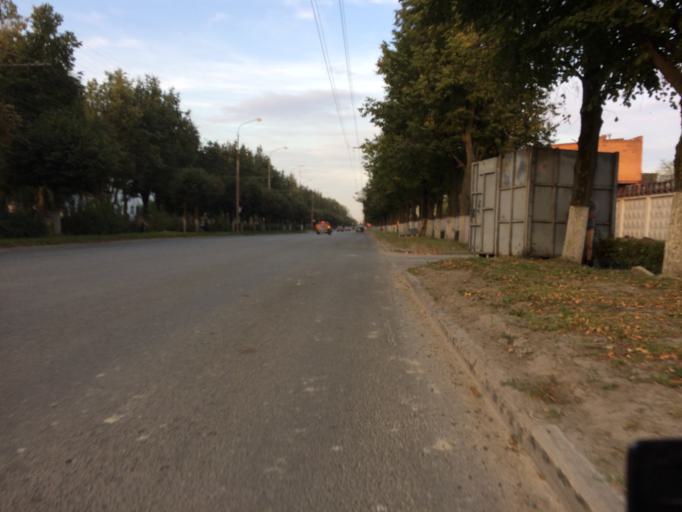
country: RU
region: Mariy-El
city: Yoshkar-Ola
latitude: 56.6341
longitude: 47.8584
